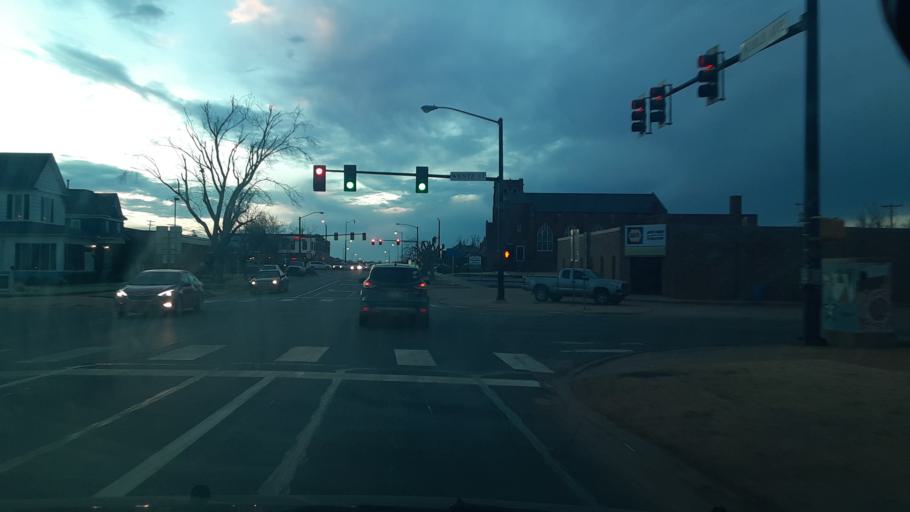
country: US
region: Oklahoma
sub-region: Logan County
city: Guthrie
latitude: 35.8802
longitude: -97.4238
